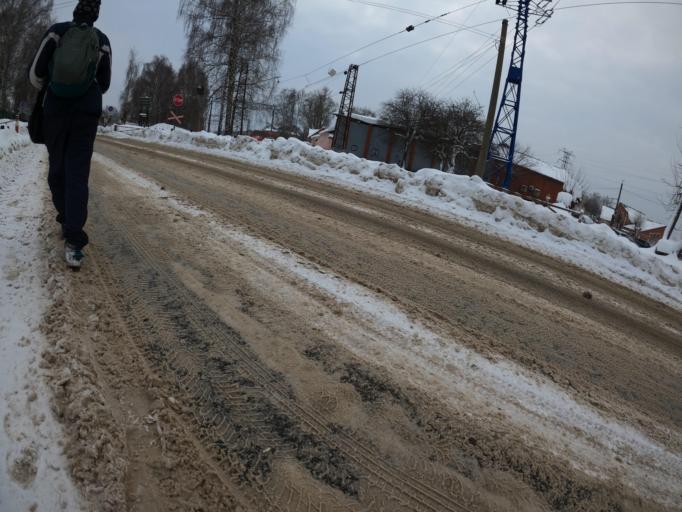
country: RU
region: Moskovskaya
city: Elektrogorsk
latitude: 55.8848
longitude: 38.7868
